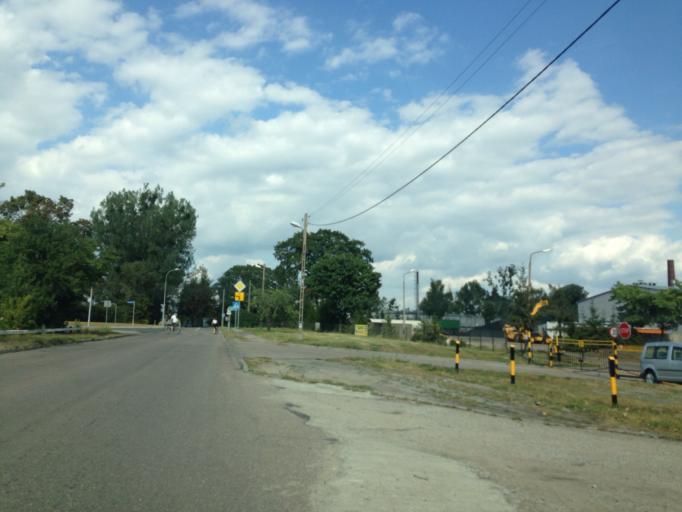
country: PL
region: Warmian-Masurian Voivodeship
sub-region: Powiat ilawski
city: Ilawa
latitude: 53.5810
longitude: 19.5693
